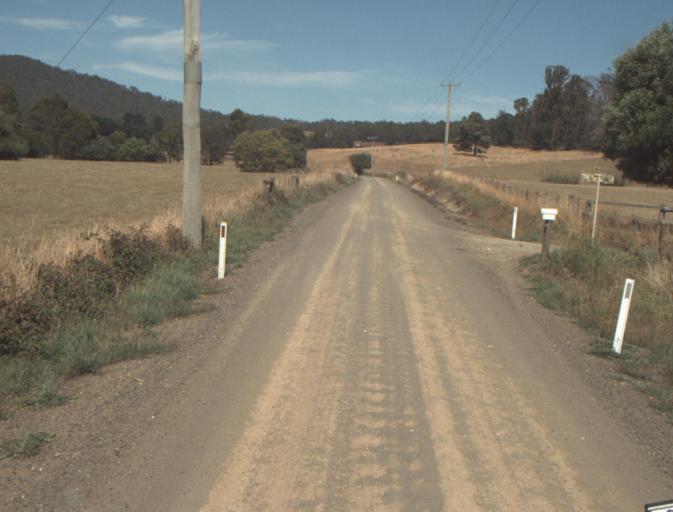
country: AU
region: Tasmania
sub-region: Launceston
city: Mayfield
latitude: -41.2542
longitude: 147.1332
